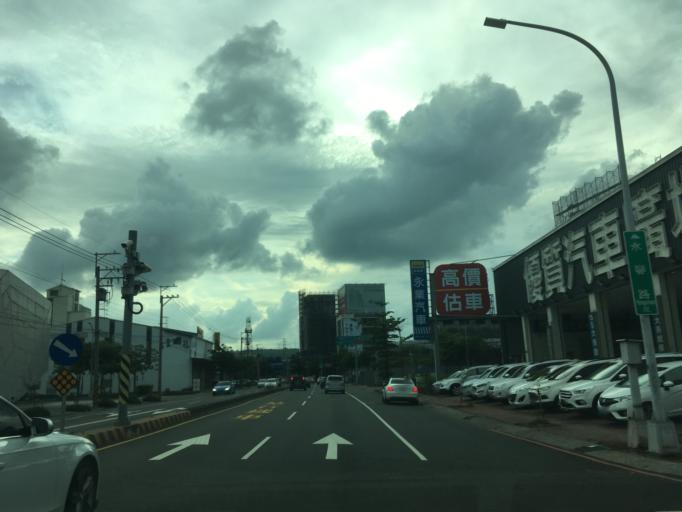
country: TW
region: Taiwan
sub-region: Taichung City
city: Taichung
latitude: 24.1405
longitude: 120.6263
